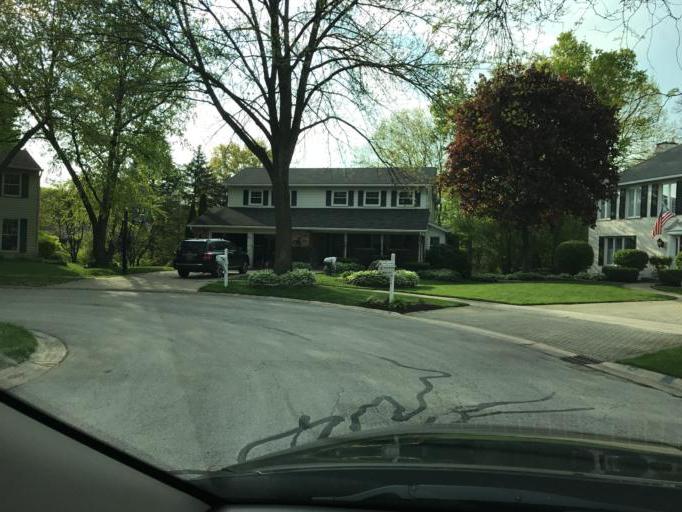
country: US
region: Illinois
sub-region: DuPage County
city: Naperville
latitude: 41.7603
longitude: -88.1166
